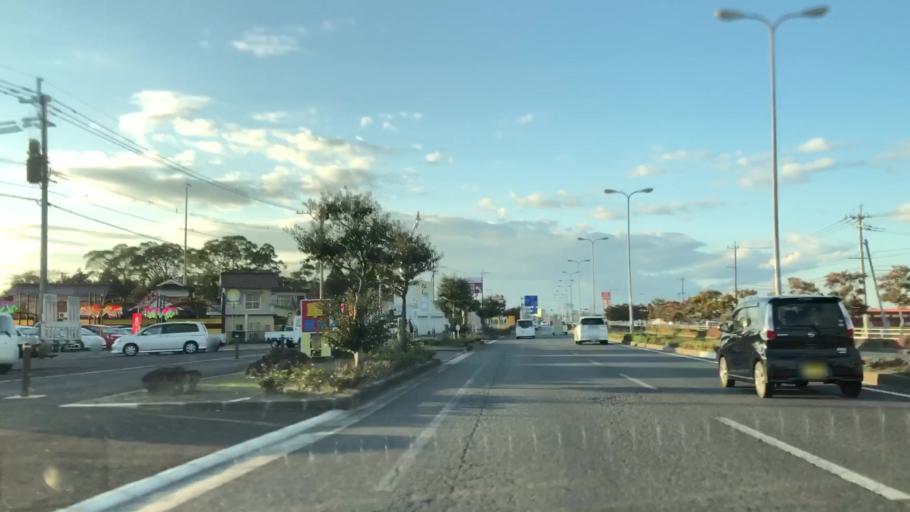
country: JP
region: Fukuoka
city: Nakatsu
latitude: 33.5487
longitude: 131.2779
